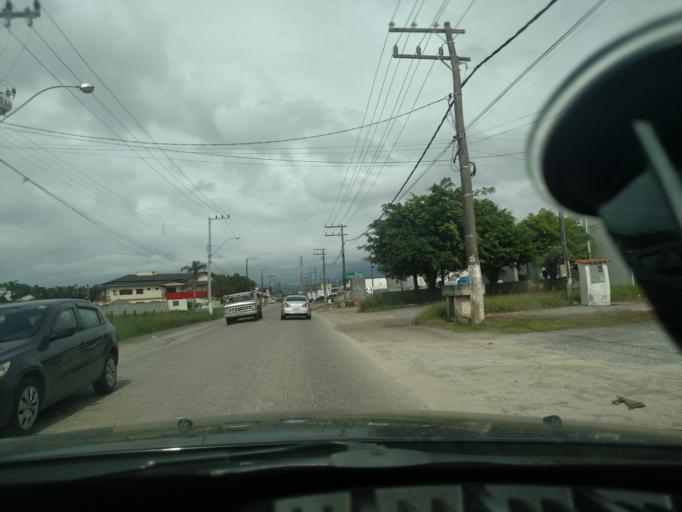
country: BR
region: Santa Catarina
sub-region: Porto Belo
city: Porto Belo
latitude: -27.1606
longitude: -48.5759
